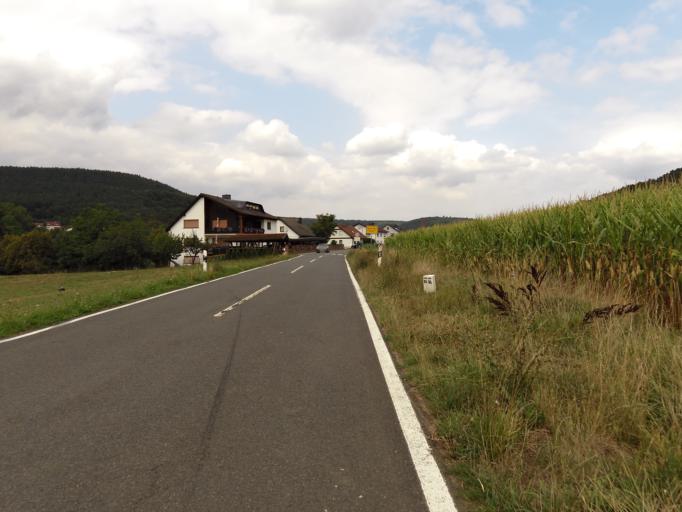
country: DE
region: Hesse
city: Hochst im Odenwald
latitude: 49.8035
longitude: 9.0075
